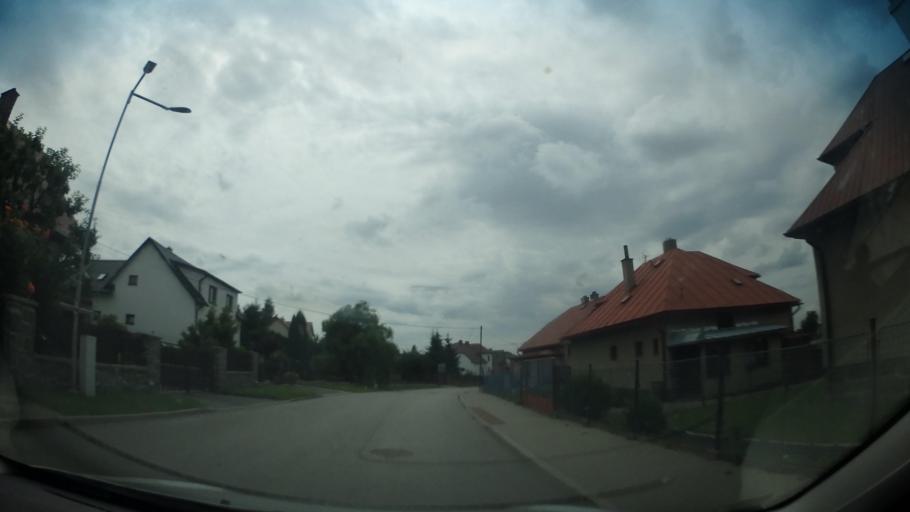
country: CZ
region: Vysocina
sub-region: Okres Zd'ar nad Sazavou
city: Nove Mesto na Morave
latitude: 49.5779
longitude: 16.0791
